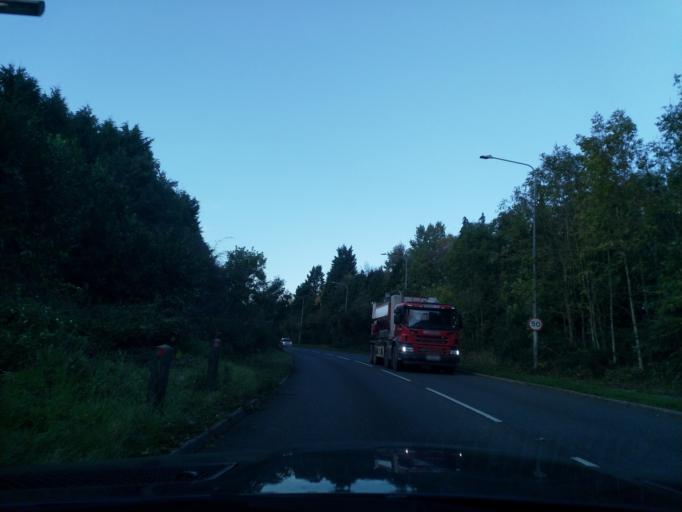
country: GB
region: England
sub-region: Warwickshire
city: Henley in Arden
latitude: 52.3362
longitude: -1.7721
